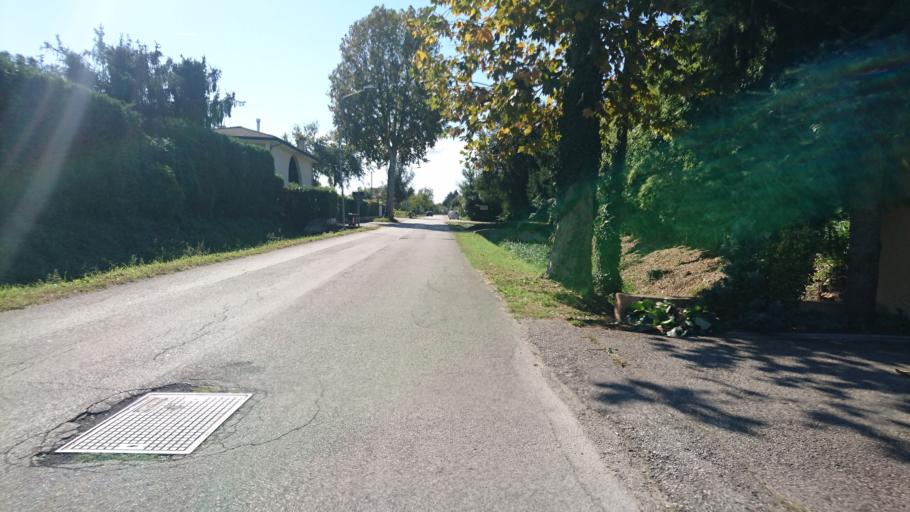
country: IT
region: Veneto
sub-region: Provincia di Venezia
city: Vigonovo
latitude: 45.3967
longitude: 12.0031
